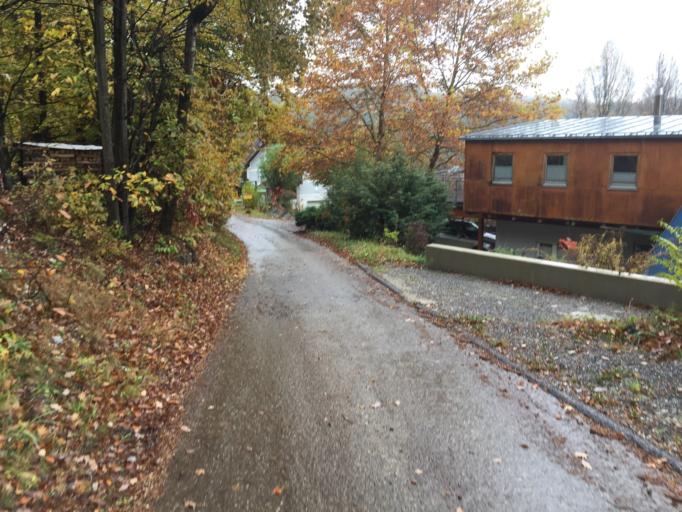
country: AT
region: Styria
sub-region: Politischer Bezirk Graz-Umgebung
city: Hart bei Graz
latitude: 47.0741
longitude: 15.5430
